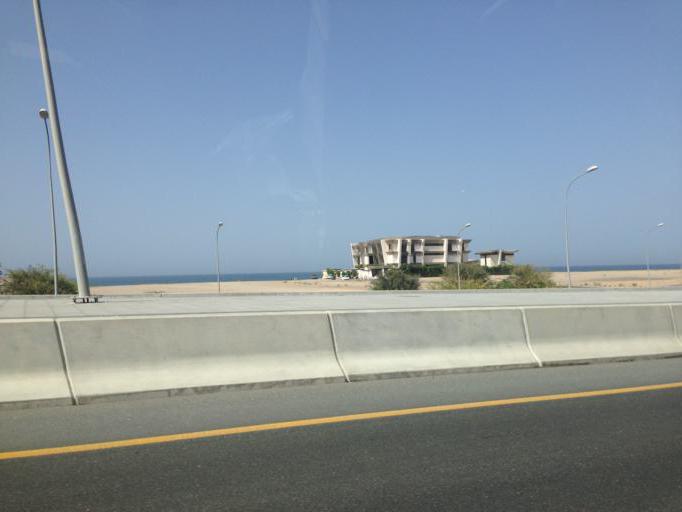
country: OM
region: Muhafazat Masqat
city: Bawshar
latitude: 23.6078
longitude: 58.3138
